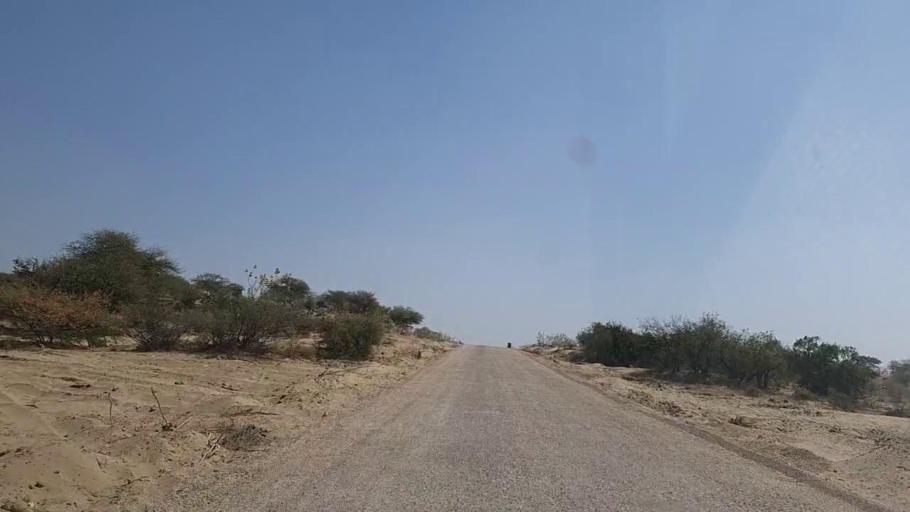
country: PK
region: Sindh
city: Diplo
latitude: 24.4802
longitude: 69.4977
